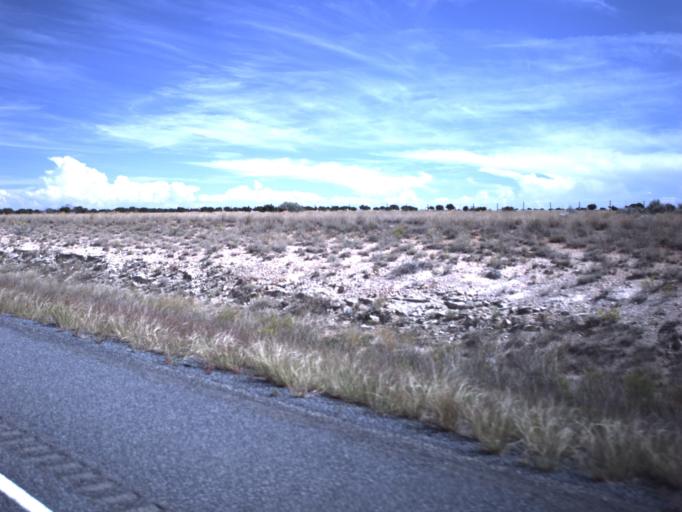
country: US
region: Utah
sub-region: Emery County
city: Castle Dale
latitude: 38.8972
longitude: -110.5911
